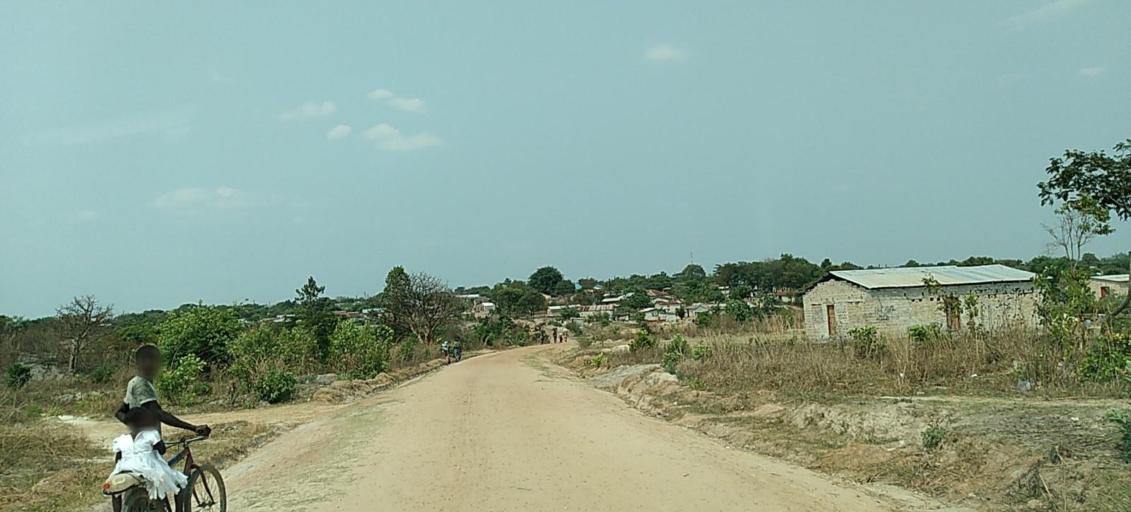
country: ZM
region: Copperbelt
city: Chambishi
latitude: -12.6246
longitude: 28.0810
